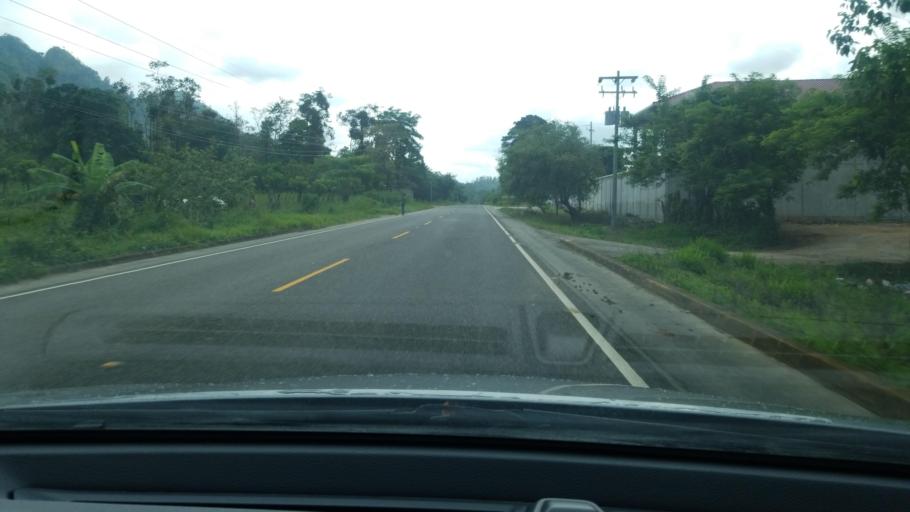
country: HN
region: Cortes
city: Potrerillos
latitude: 15.6163
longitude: -88.2752
